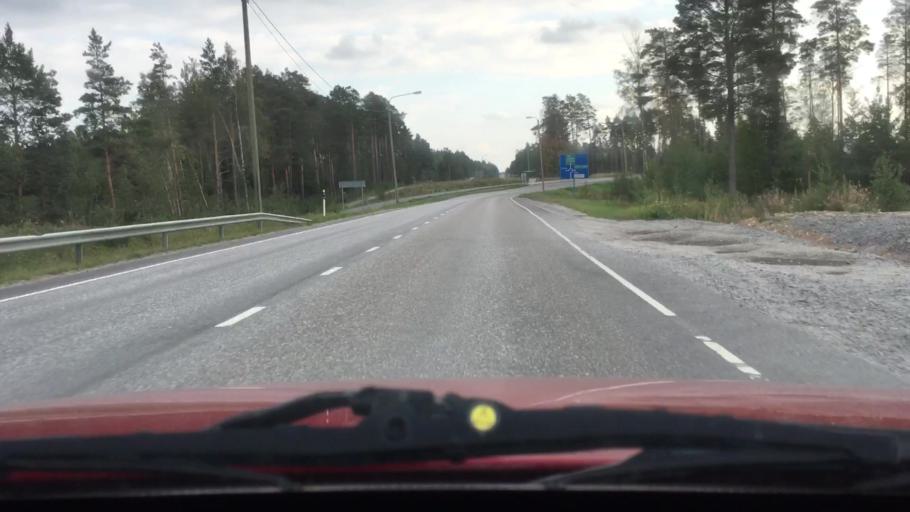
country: FI
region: Varsinais-Suomi
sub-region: Turku
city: Masku
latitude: 60.5447
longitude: 22.1284
